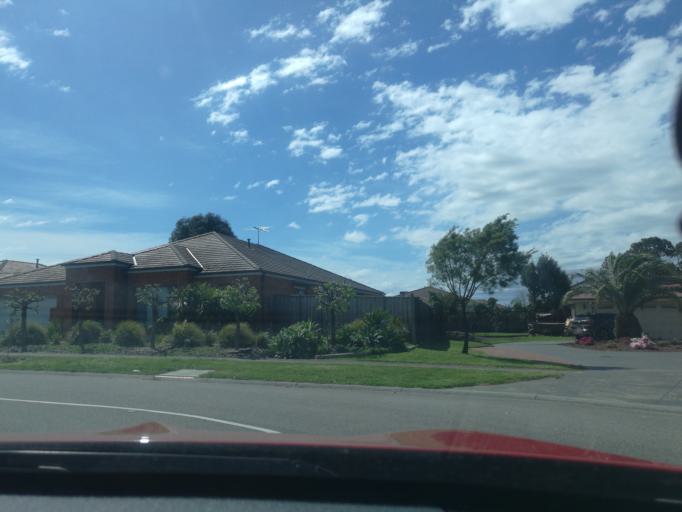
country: AU
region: Victoria
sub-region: Casey
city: Lynbrook
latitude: -38.0674
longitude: 145.2482
